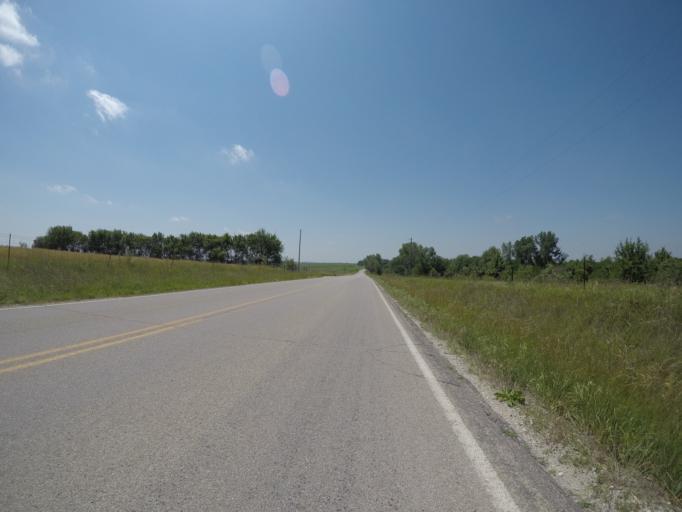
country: US
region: Kansas
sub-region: Pottawatomie County
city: Westmoreland
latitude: 39.3128
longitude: -96.4362
